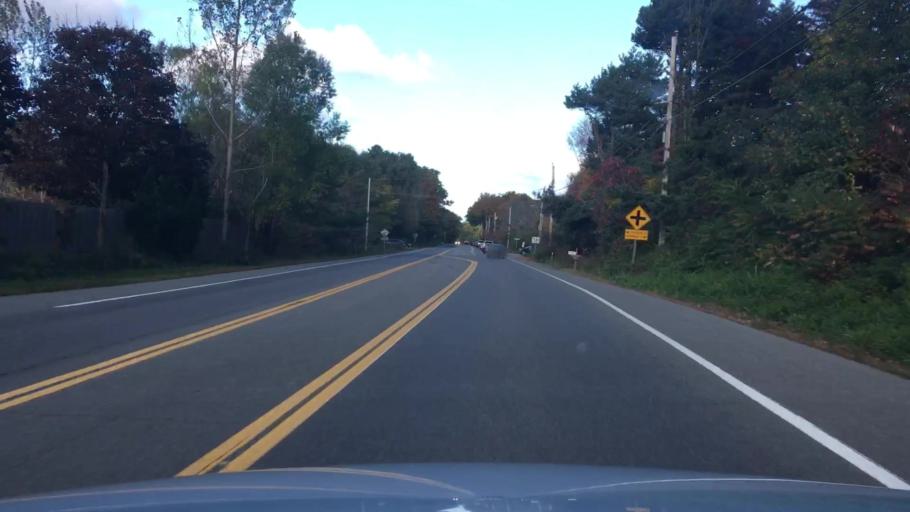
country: US
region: New Hampshire
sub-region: Strafford County
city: Durham
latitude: 43.1354
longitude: -70.8910
